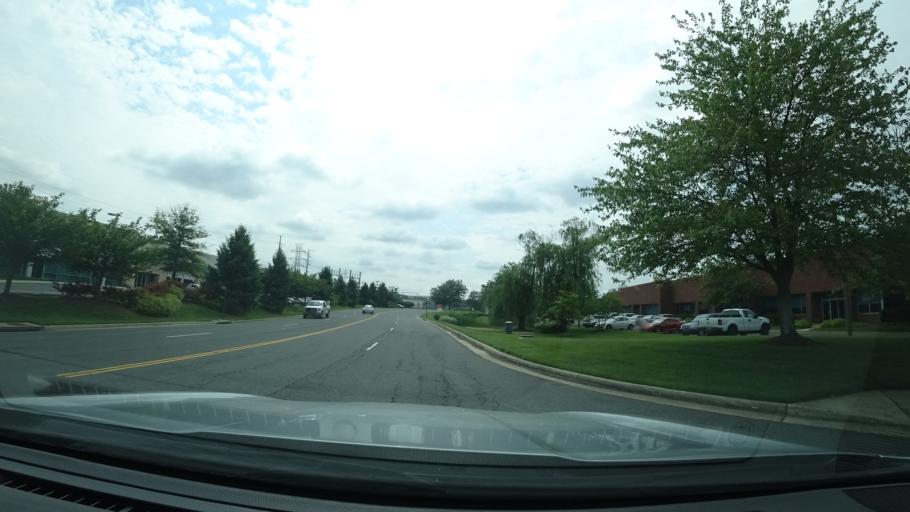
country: US
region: Virginia
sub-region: Loudoun County
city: Sterling
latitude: 38.9957
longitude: -77.4232
